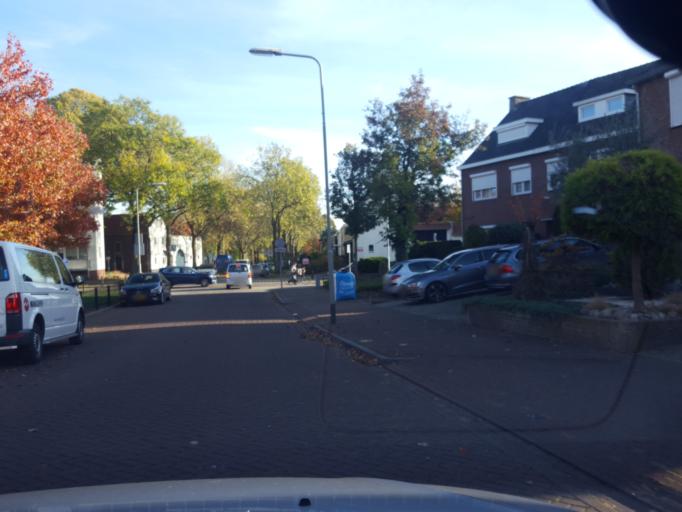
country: NL
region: Limburg
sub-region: Gemeente Beek
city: Beek
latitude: 50.9638
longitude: 5.8176
